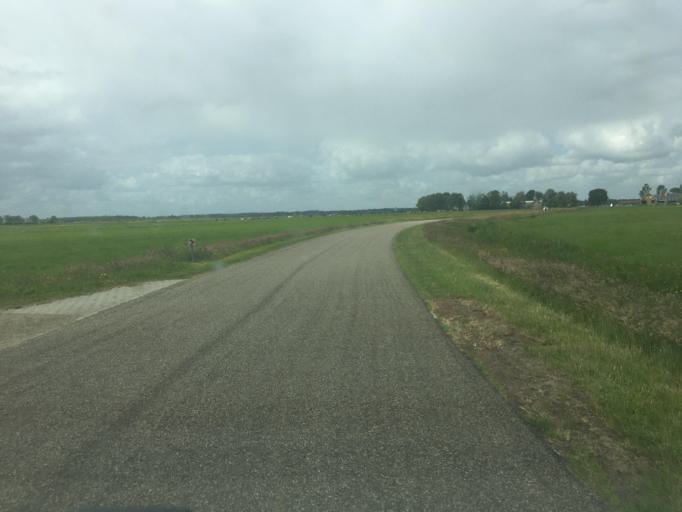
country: NL
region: Friesland
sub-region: Gemeente Heerenveen
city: Nieuwehorne
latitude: 52.9226
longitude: 6.0356
